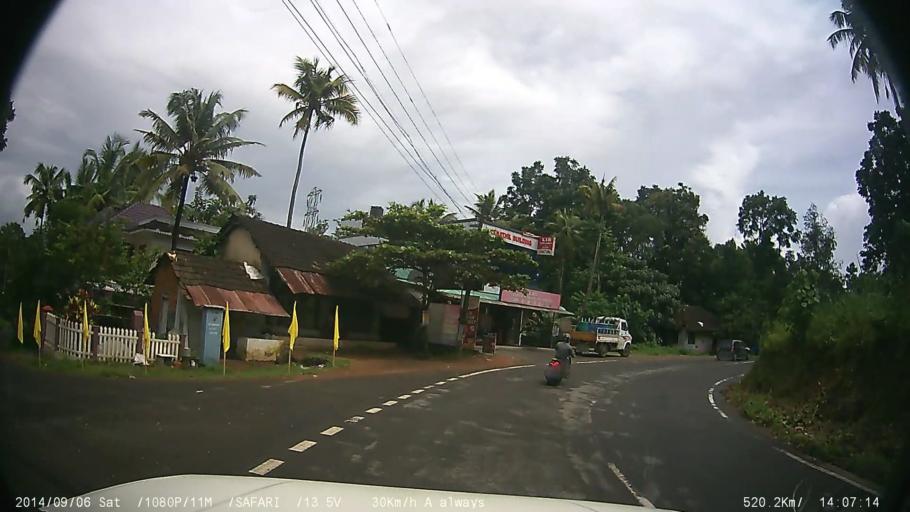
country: IN
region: Kerala
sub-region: Kottayam
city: Palackattumala
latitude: 9.7030
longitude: 76.5568
